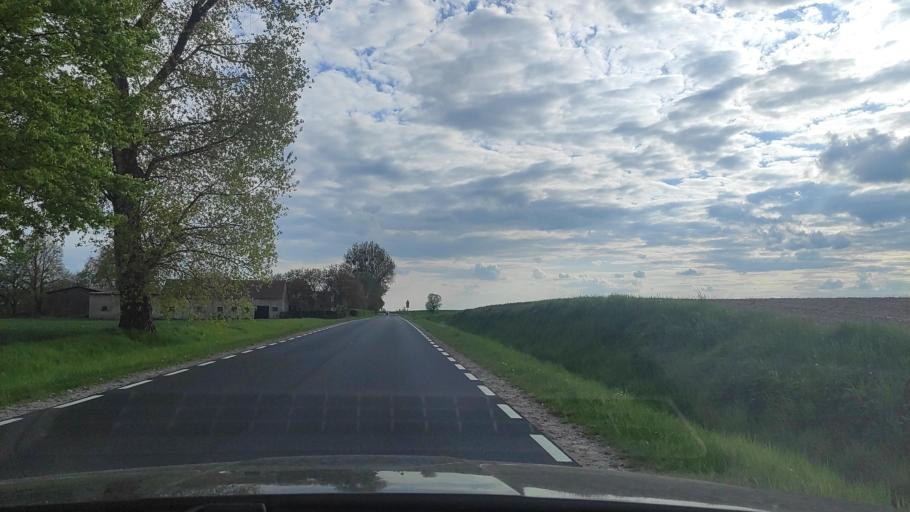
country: PL
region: Greater Poland Voivodeship
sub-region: Powiat poznanski
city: Kostrzyn
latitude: 52.4356
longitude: 17.2370
